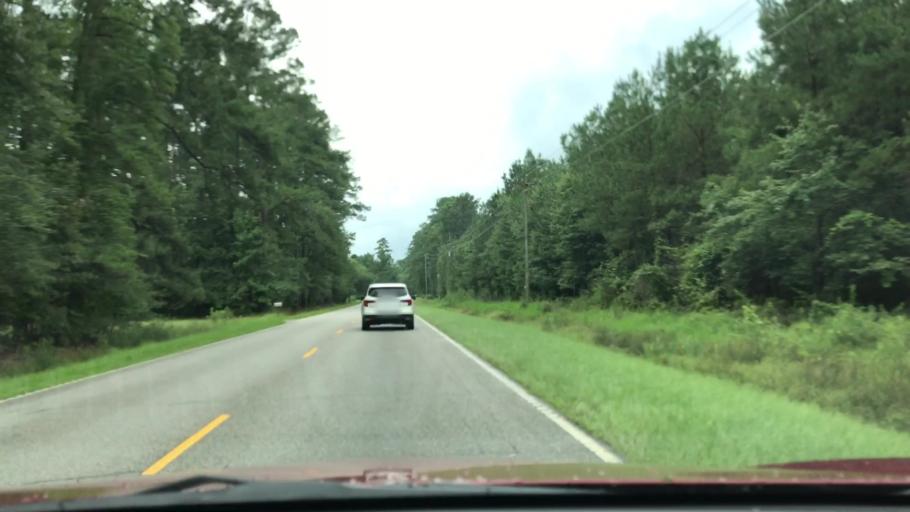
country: US
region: South Carolina
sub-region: Georgetown County
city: Murrells Inlet
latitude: 33.6233
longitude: -79.1919
